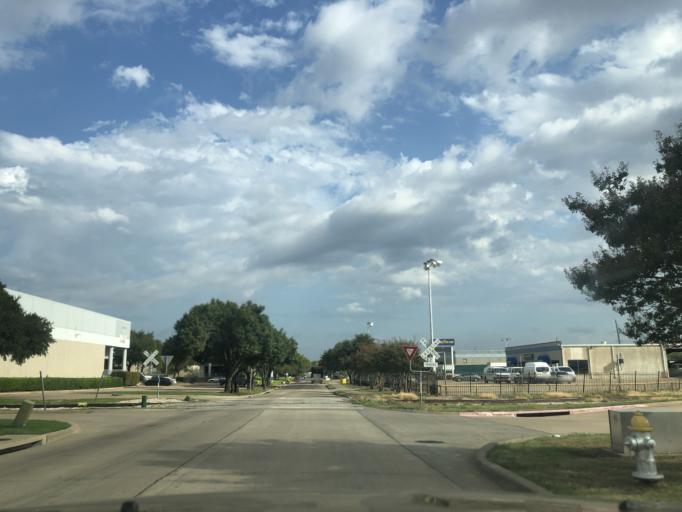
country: US
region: Texas
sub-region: Dallas County
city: Garland
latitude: 32.8823
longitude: -96.6683
